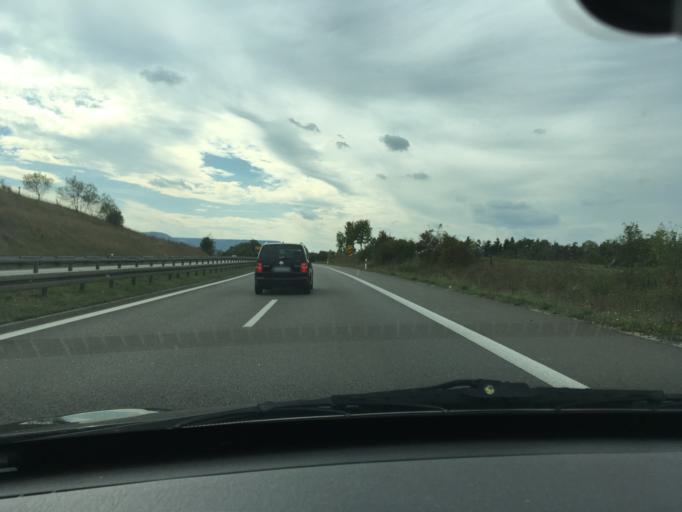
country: DE
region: Baden-Wuerttemberg
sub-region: Tuebingen Region
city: Dusslingen
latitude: 48.4636
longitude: 9.0618
